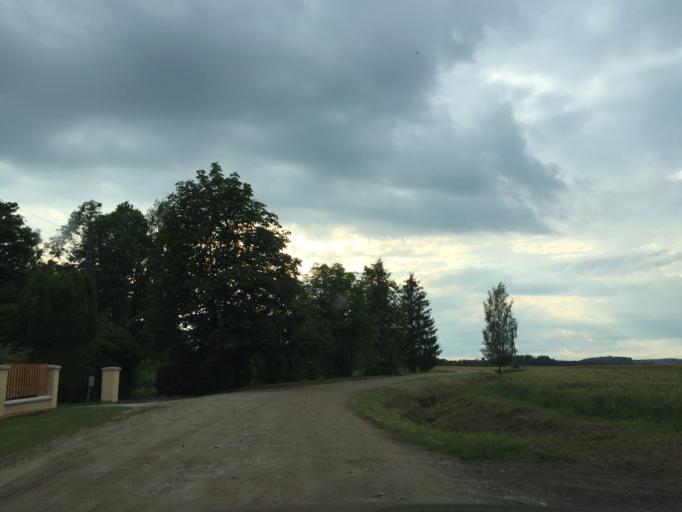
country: LV
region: Dobeles Rajons
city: Dobele
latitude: 56.5648
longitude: 23.2926
